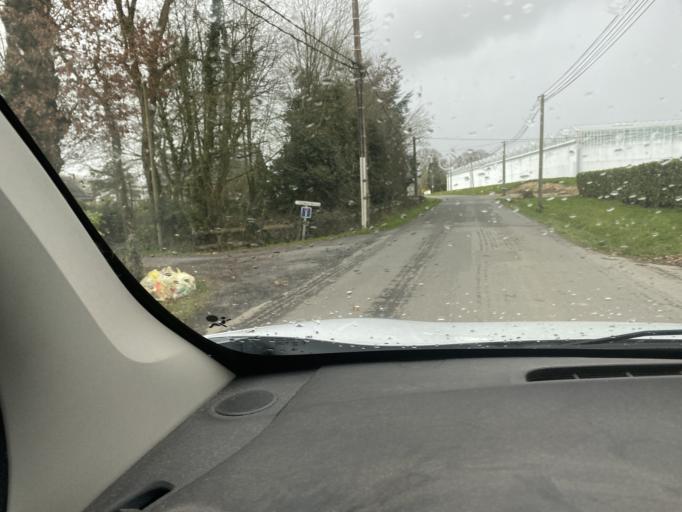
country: FR
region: Brittany
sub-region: Departement d'Ille-et-Vilaine
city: La Chapelle-des-Fougeretz
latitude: 48.1878
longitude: -1.7069
